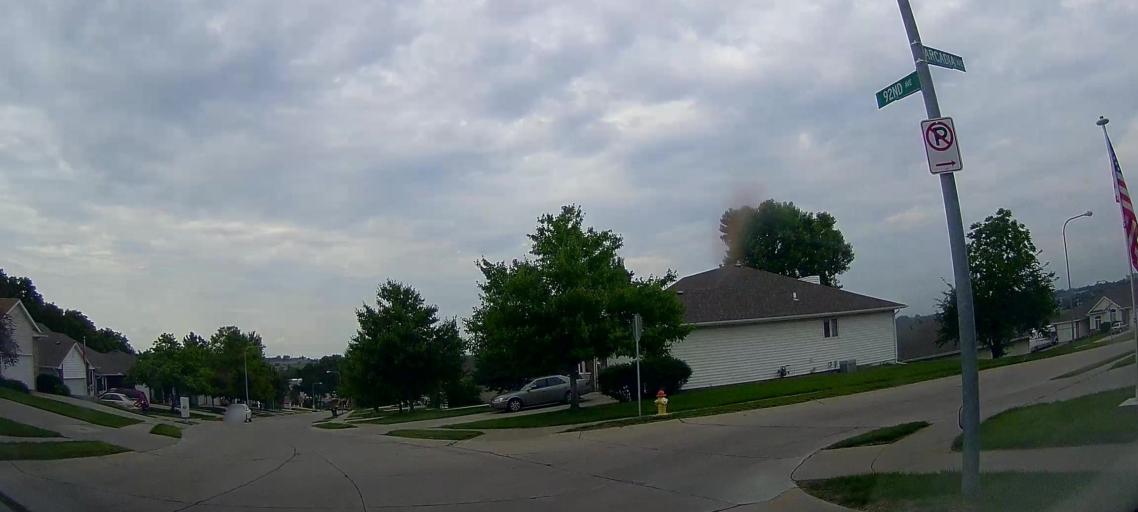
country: US
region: Nebraska
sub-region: Douglas County
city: Ralston
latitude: 41.3116
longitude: -96.0563
